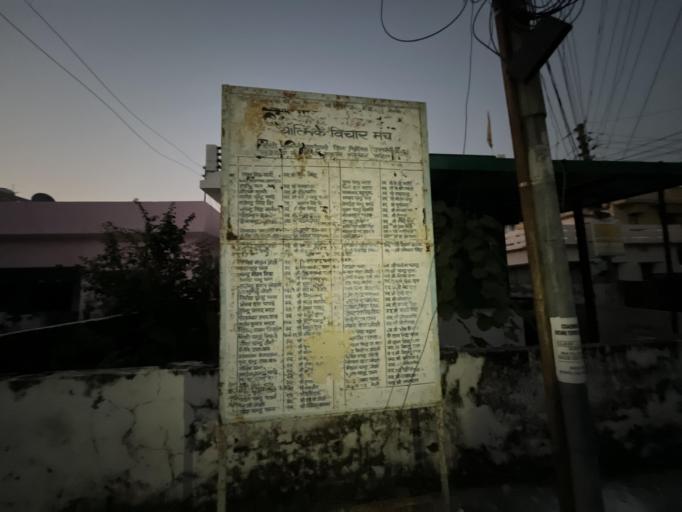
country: IN
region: Uttarakhand
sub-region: Naini Tal
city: Haldwani
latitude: 29.2163
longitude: 79.5161
